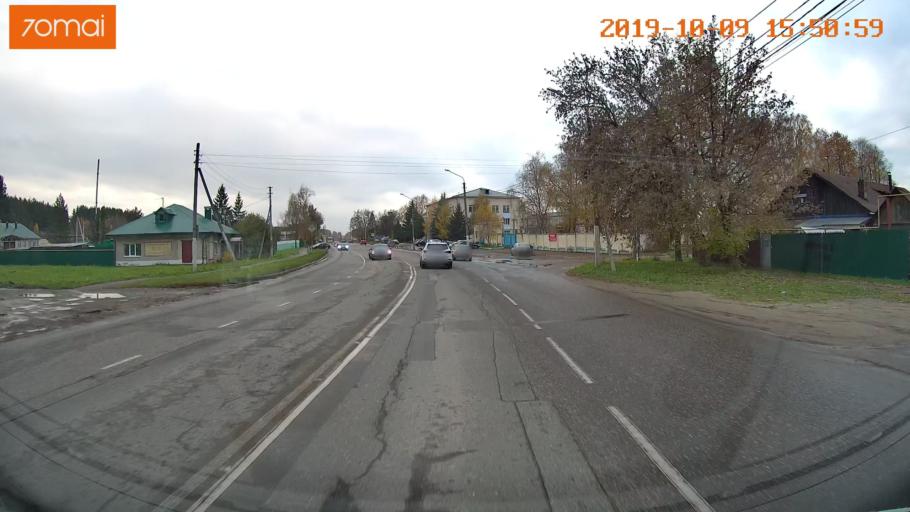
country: RU
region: Kostroma
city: Oktyabr'skiy
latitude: 57.8003
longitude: 40.9834
